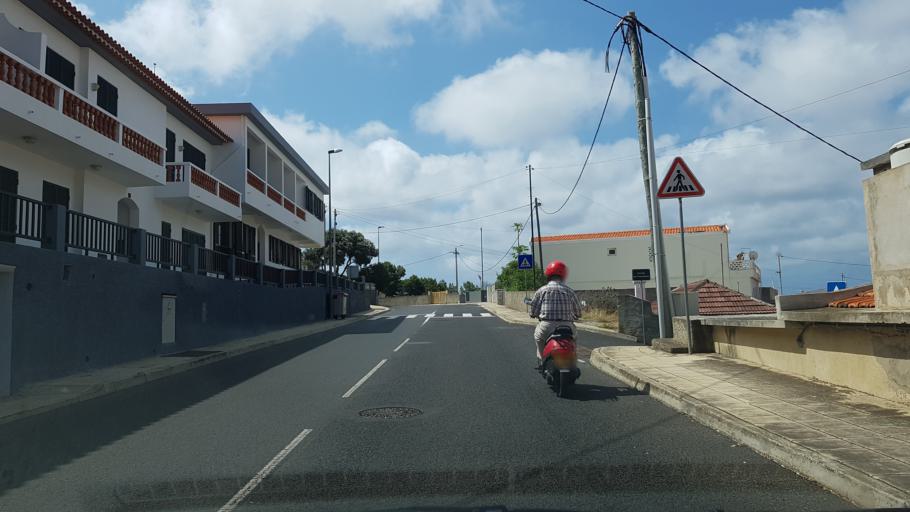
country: PT
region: Madeira
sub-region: Porto Santo
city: Vila de Porto Santo
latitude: 33.0650
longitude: -16.3340
